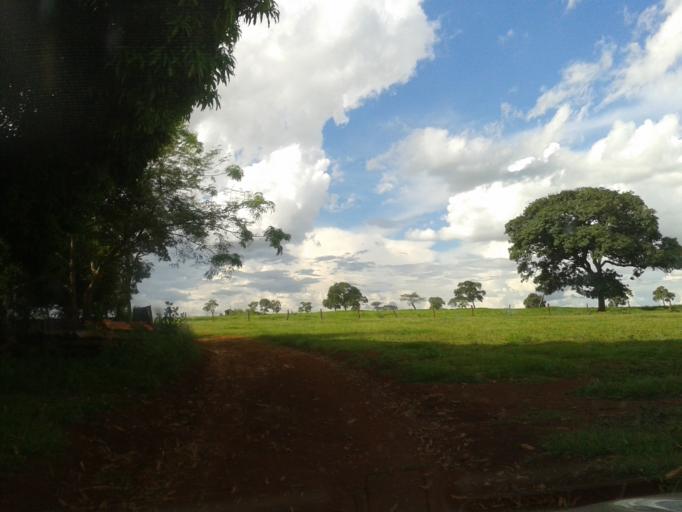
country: BR
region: Minas Gerais
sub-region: Capinopolis
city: Capinopolis
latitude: -18.7640
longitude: -49.8249
